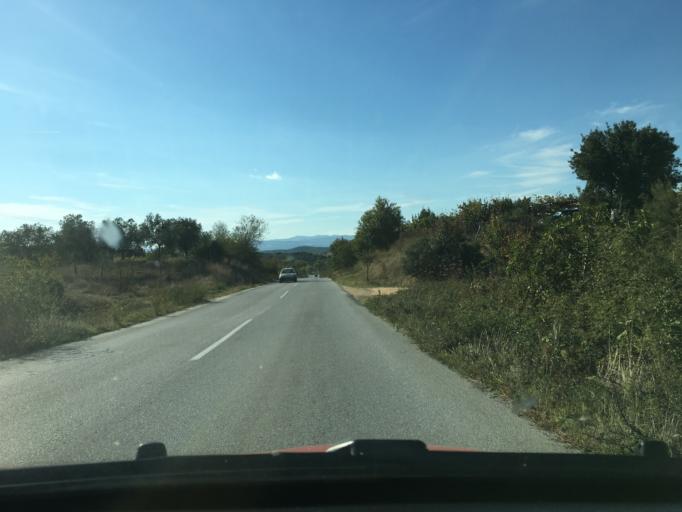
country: GR
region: Central Macedonia
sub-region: Nomos Chalkidikis
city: Megali Panagia
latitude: 40.3855
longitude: 23.7173
